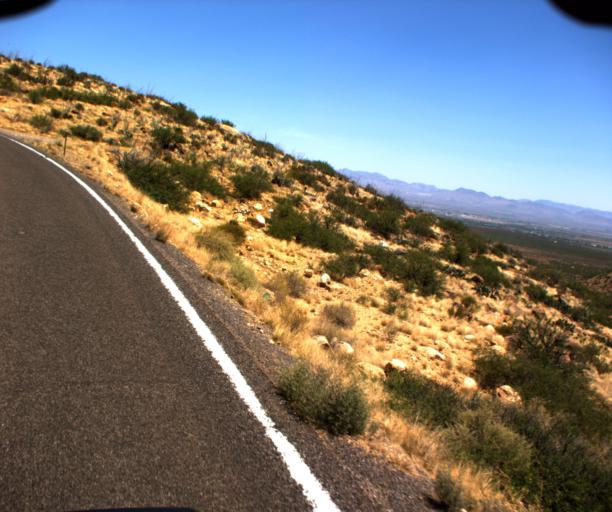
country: US
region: Arizona
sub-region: Graham County
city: Swift Trail Junction
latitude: 32.6892
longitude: -109.7601
